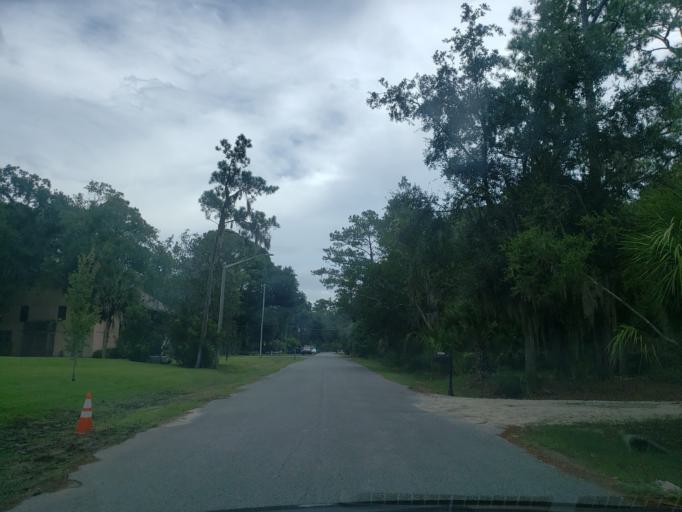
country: US
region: Georgia
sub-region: Chatham County
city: Wilmington Island
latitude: 32.0058
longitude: -80.9597
